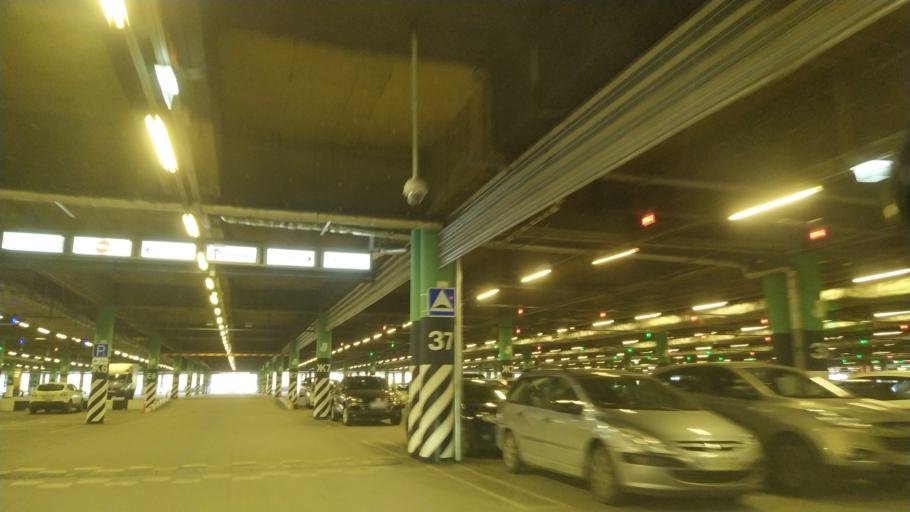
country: RU
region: Leningrad
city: Bugry
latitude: 60.0912
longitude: 30.3808
